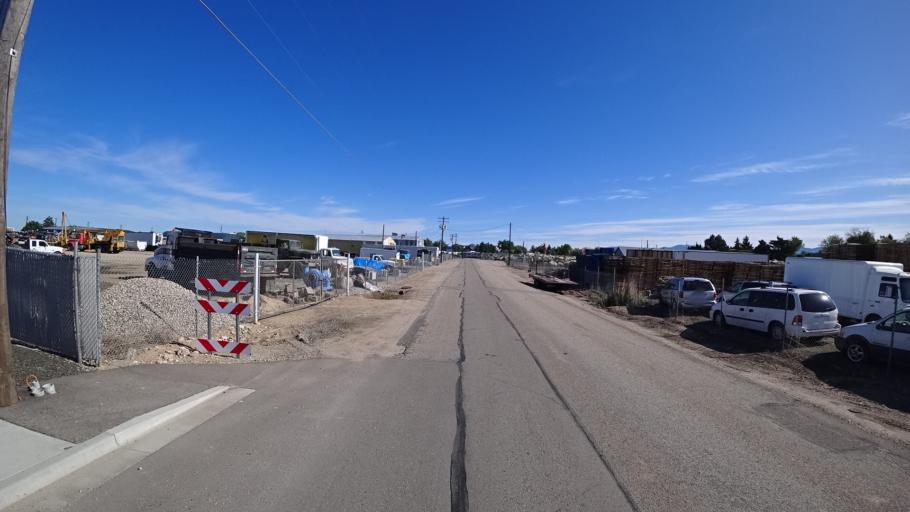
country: US
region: Idaho
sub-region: Ada County
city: Garden City
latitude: 43.5813
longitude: -116.2611
